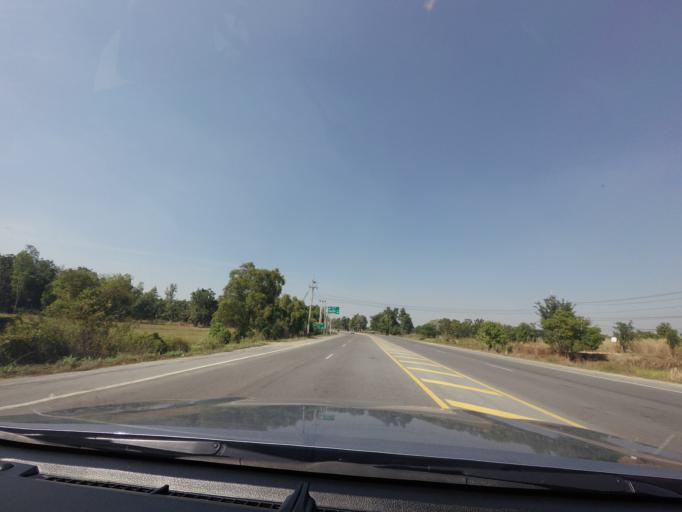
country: TH
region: Sukhothai
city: Ban Na
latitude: 17.0545
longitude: 99.7185
